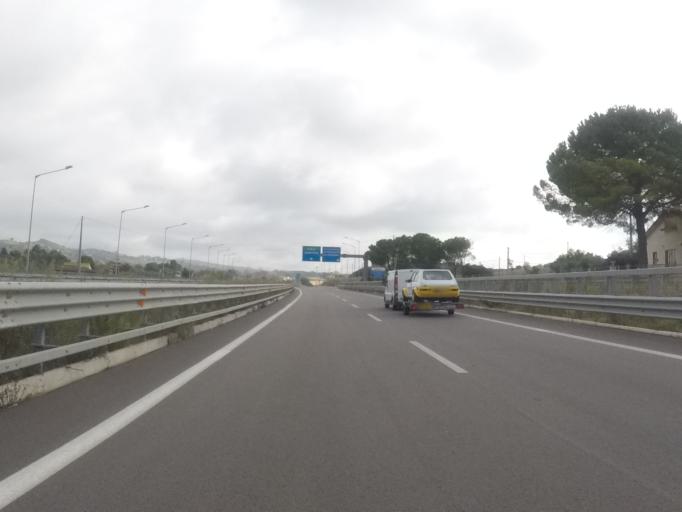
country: IT
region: Sicily
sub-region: Agrigento
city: Grotte
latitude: 37.3722
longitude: 13.7137
